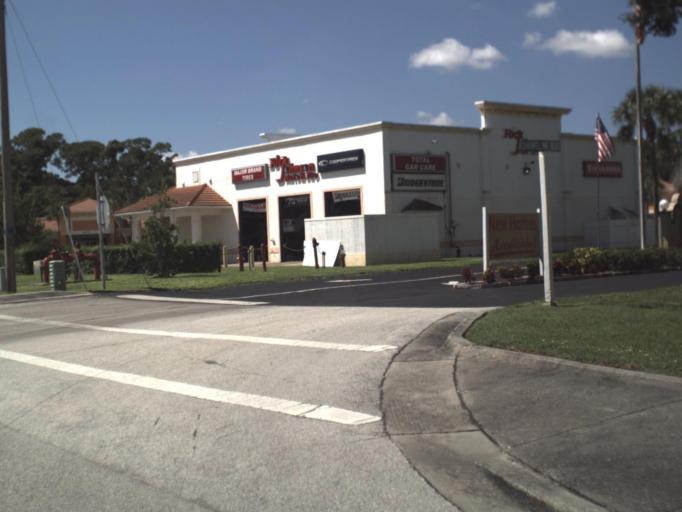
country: US
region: Florida
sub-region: Lee County
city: Suncoast Estates
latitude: 26.6906
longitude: -81.8612
